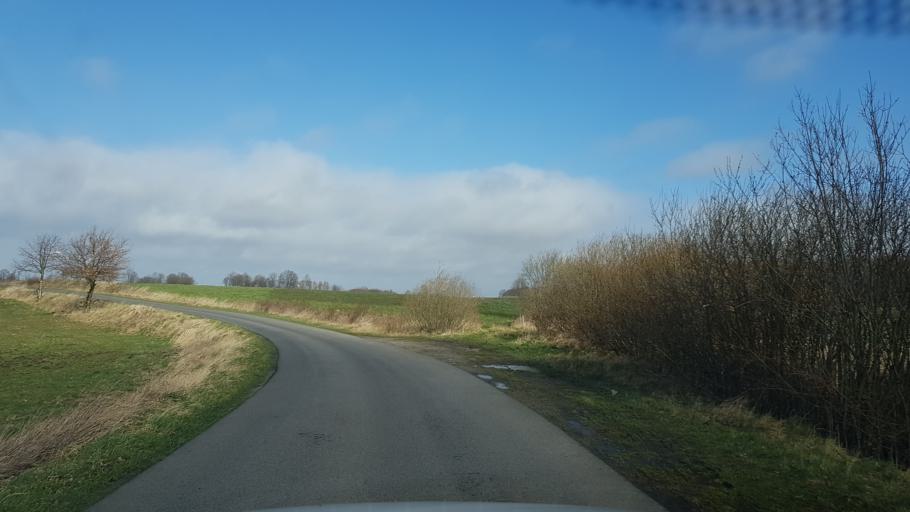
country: PL
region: West Pomeranian Voivodeship
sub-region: Powiat slawienski
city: Slawno
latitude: 54.4832
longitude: 16.6536
